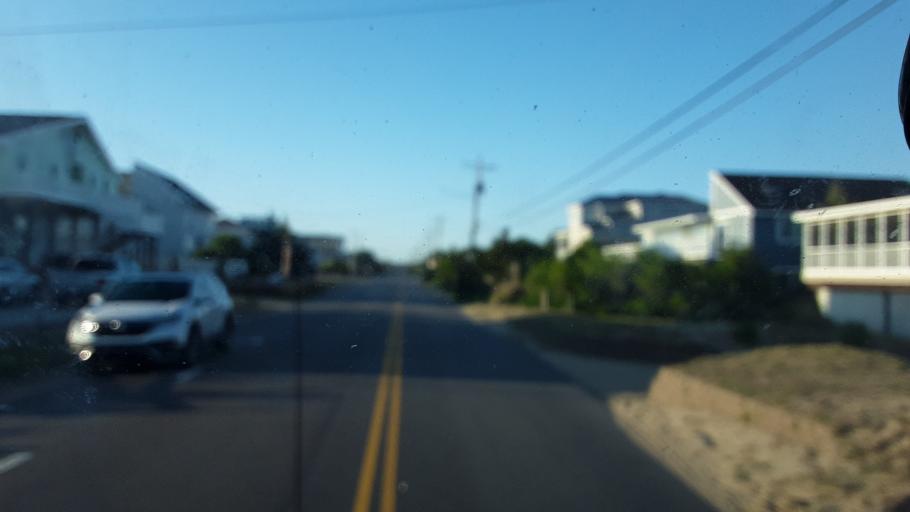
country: US
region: Virginia
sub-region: City of Virginia Beach
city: Virginia Beach
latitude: 36.7133
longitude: -75.9320
